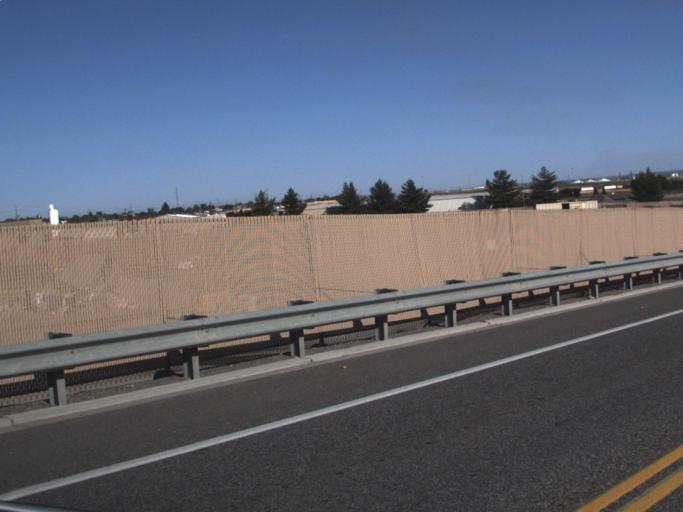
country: US
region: Washington
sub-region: Franklin County
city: Pasco
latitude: 46.2213
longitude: -119.0902
